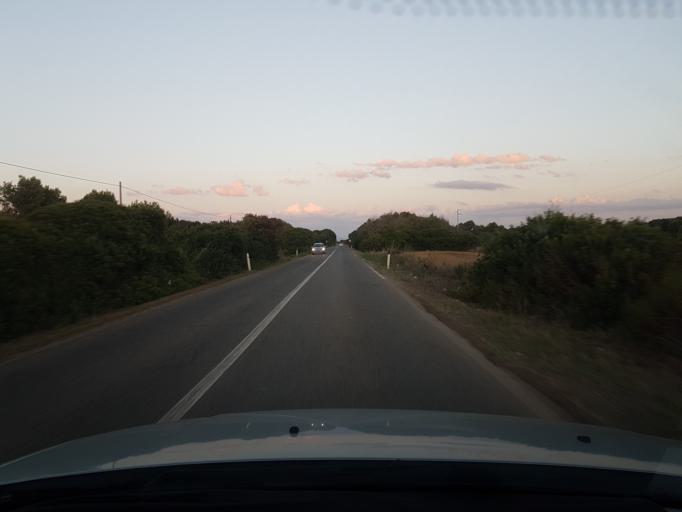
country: IT
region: Sardinia
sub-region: Provincia di Oristano
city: Riola Sardo
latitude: 40.0248
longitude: 8.4409
